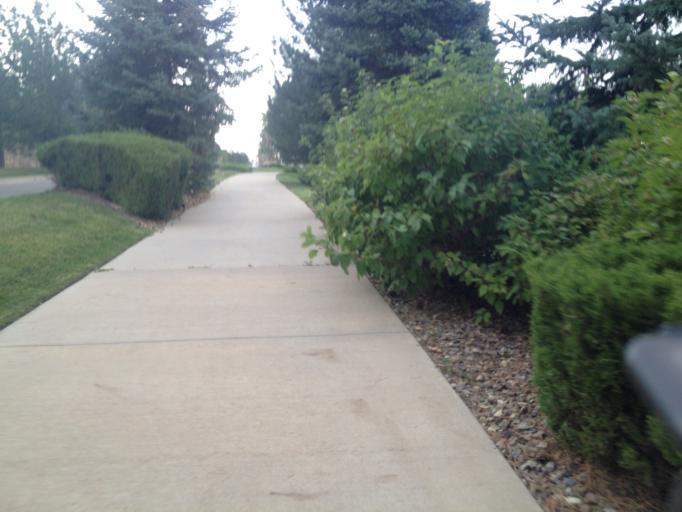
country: US
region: Colorado
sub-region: Boulder County
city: Superior
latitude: 39.9311
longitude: -105.1372
